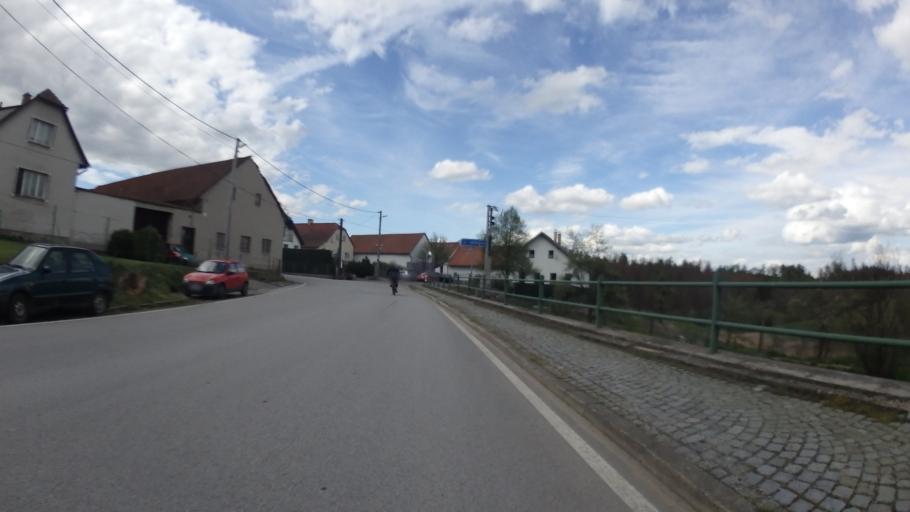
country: CZ
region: Vysocina
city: Merin
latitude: 49.3633
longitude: 15.9065
